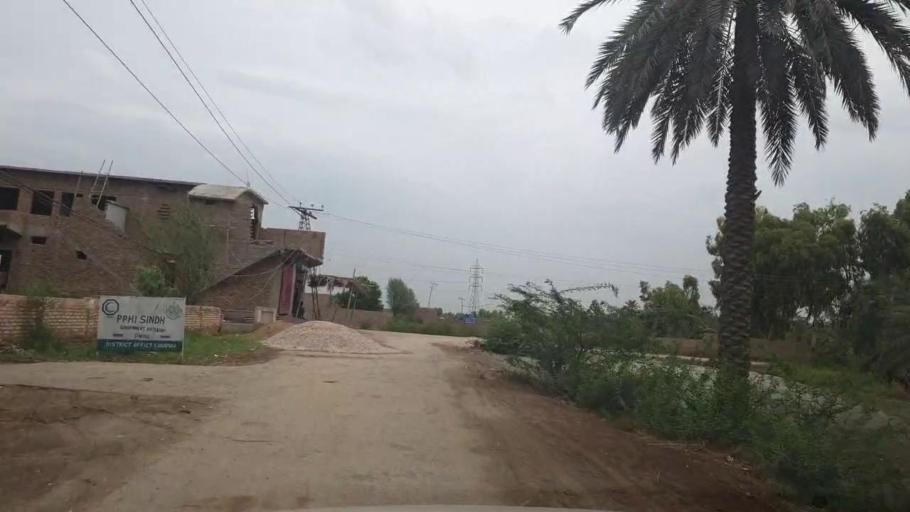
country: PK
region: Sindh
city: Khairpur
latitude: 27.5479
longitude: 68.7393
